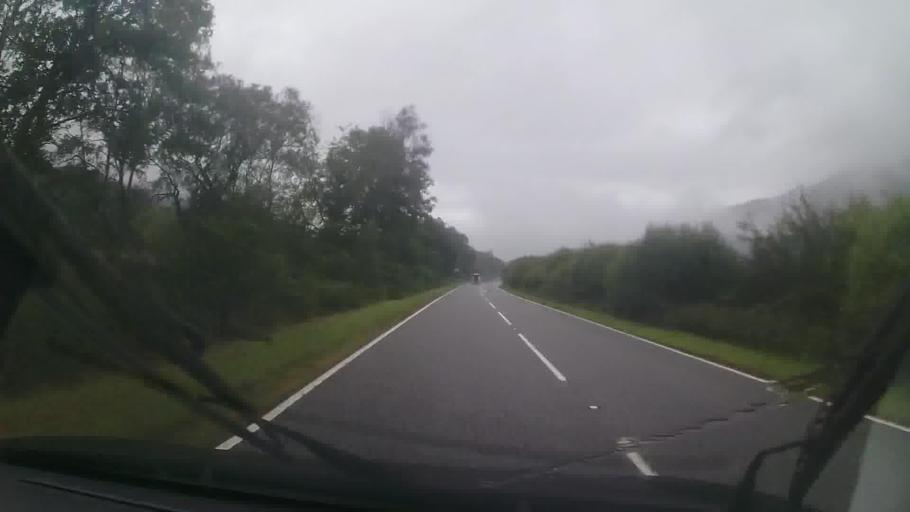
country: GB
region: Scotland
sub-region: Highland
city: Fort William
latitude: 56.6686
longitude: -5.0778
